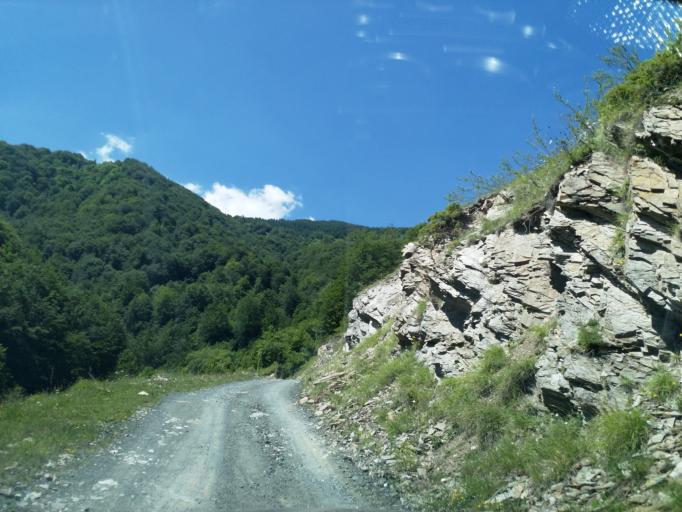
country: XK
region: Mitrovica
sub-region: Komuna e Leposaviqit
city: Leposaviq
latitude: 43.2669
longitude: 20.8598
